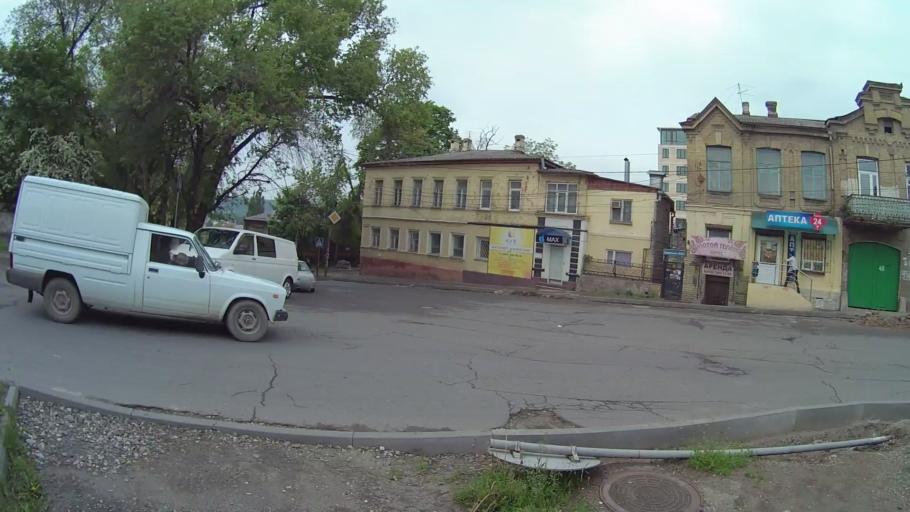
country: RU
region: Stavropol'skiy
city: Goryachevodskiy
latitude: 44.0352
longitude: 43.0756
